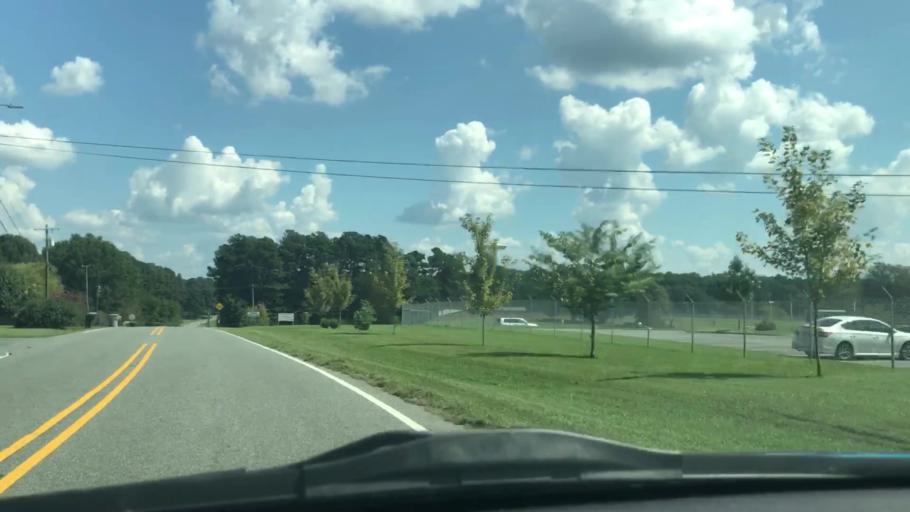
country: US
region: North Carolina
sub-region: Randolph County
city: Asheboro
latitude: 35.7496
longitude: -79.8175
